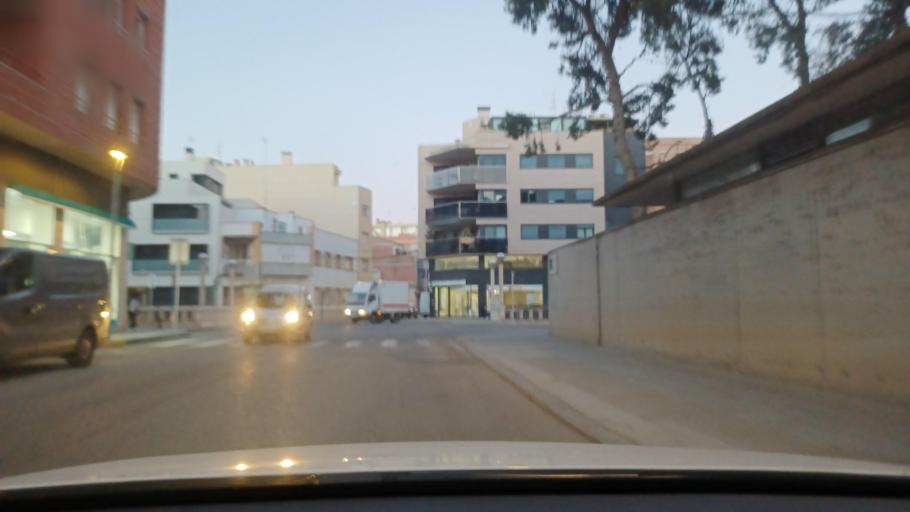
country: ES
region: Catalonia
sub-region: Provincia de Tarragona
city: Amposta
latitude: 40.7107
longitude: 0.5816
